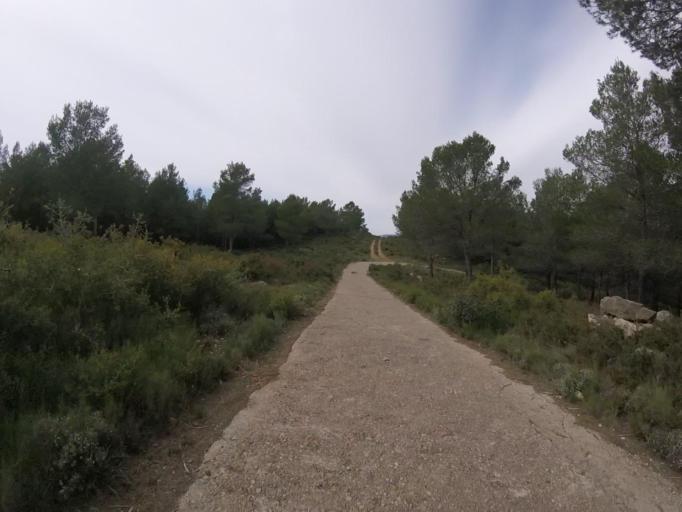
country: ES
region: Valencia
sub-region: Provincia de Castello
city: Cabanes
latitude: 40.1887
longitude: 0.0805
